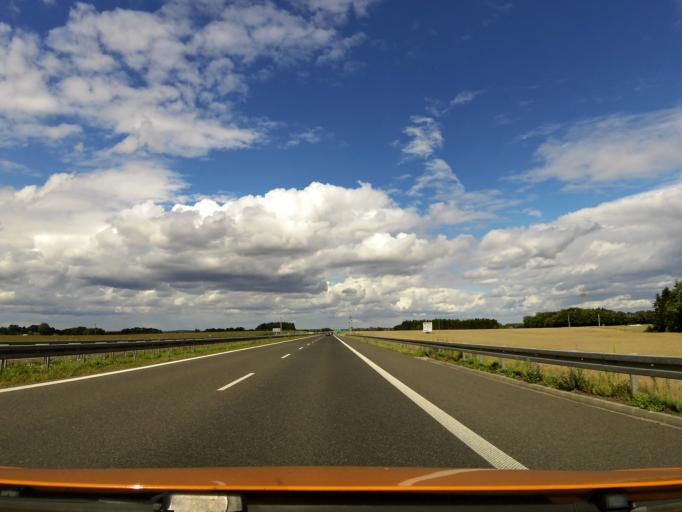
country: PL
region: West Pomeranian Voivodeship
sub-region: Powiat goleniowski
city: Nowogard
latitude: 53.6761
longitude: 15.0823
